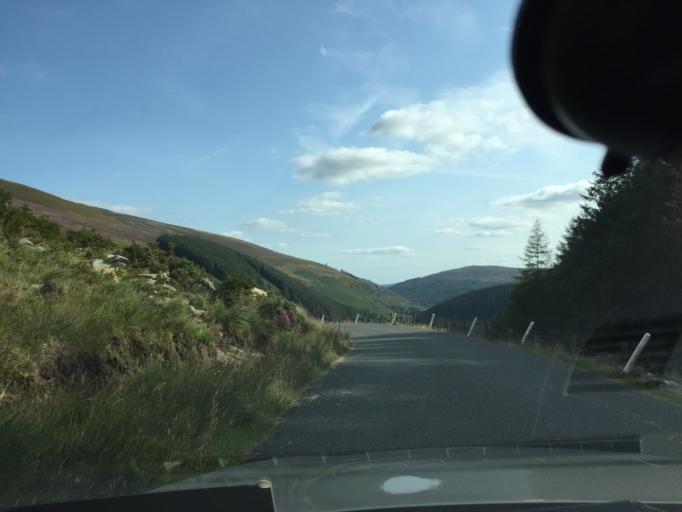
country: IE
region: Leinster
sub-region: Wicklow
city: Rathdrum
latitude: 53.0655
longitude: -6.3379
